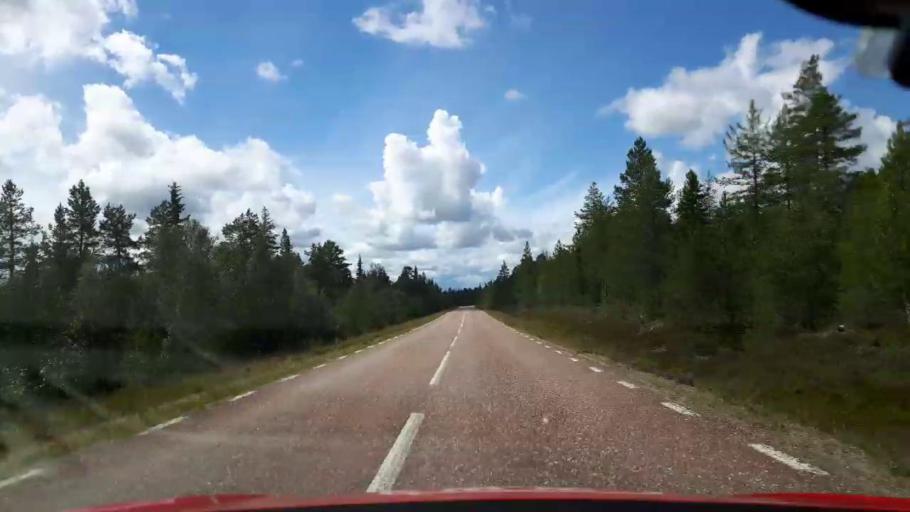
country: SE
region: Dalarna
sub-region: Alvdalens Kommun
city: AElvdalen
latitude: 61.8126
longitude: 13.5328
